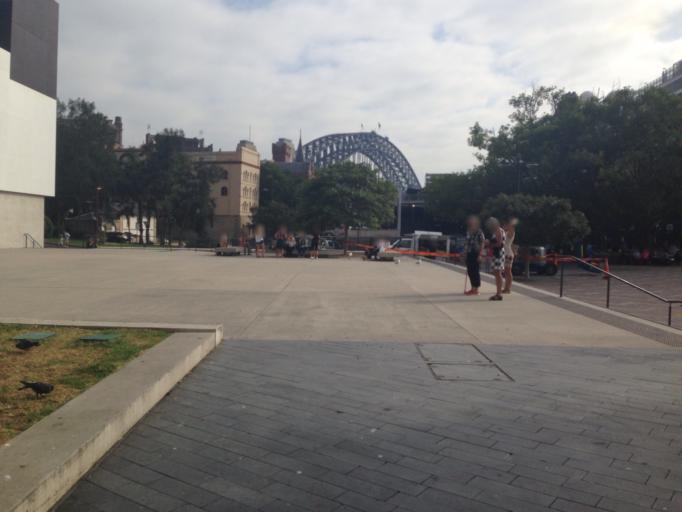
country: AU
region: New South Wales
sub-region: City of Sydney
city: Sydney
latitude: -33.8598
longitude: 151.2096
